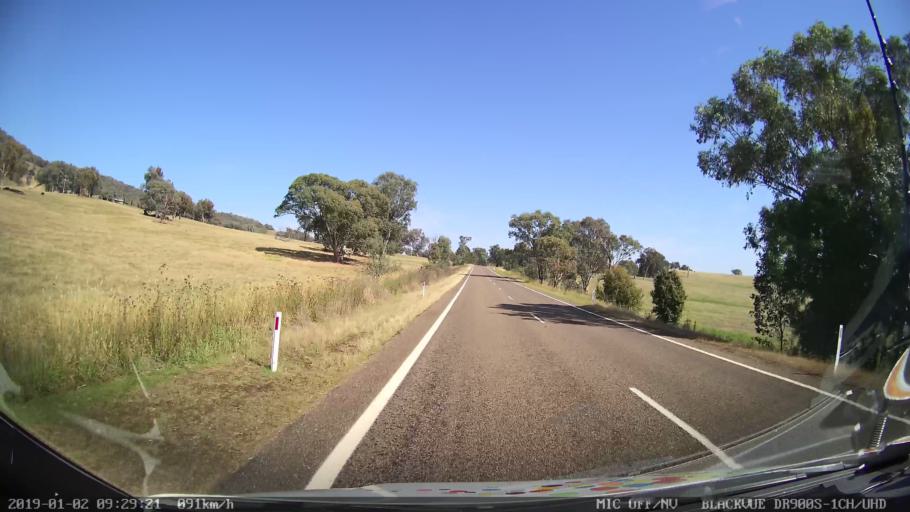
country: AU
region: New South Wales
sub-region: Tumut Shire
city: Tumut
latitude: -35.3396
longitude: 148.2433
